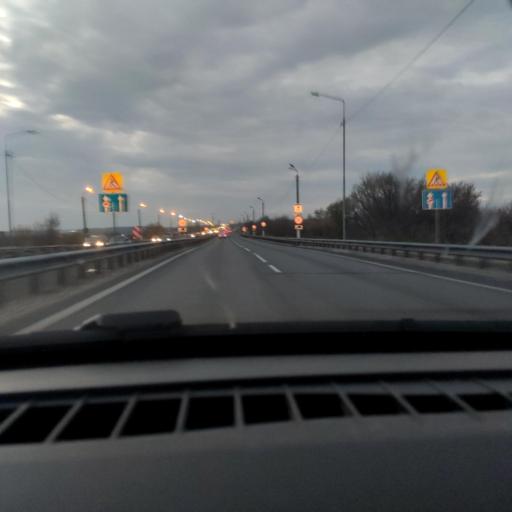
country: RU
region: Voronezj
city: Pridonskoy
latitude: 51.6501
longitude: 39.0783
